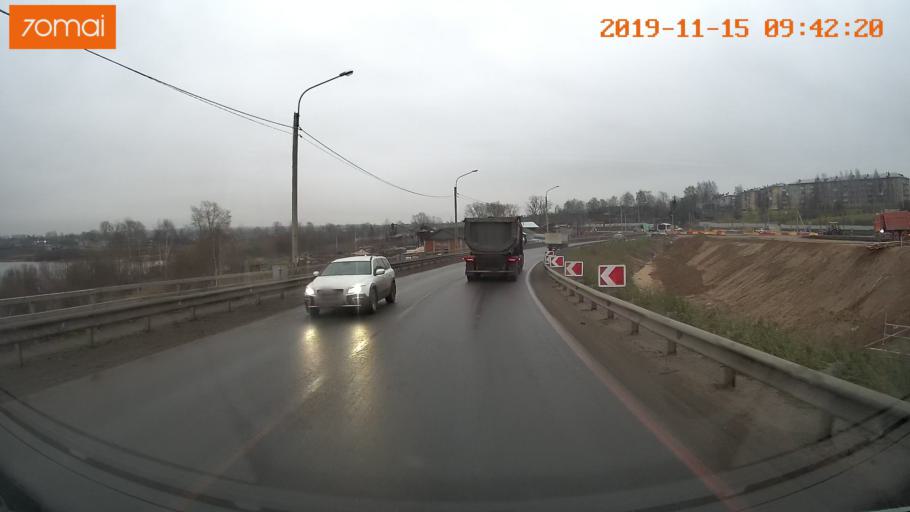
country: RU
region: Vologda
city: Sheksna
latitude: 59.2111
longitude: 38.4987
